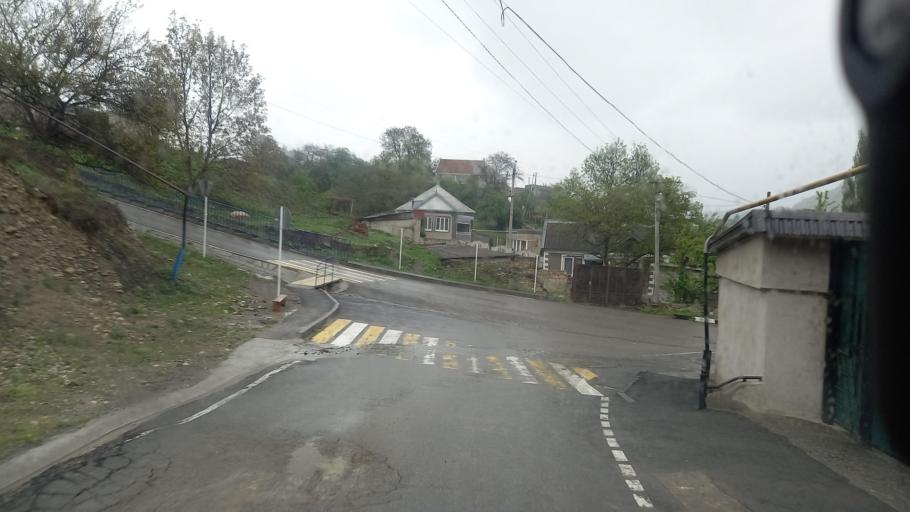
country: RU
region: Kabardino-Balkariya
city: Gundelen
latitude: 43.5972
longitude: 43.1522
